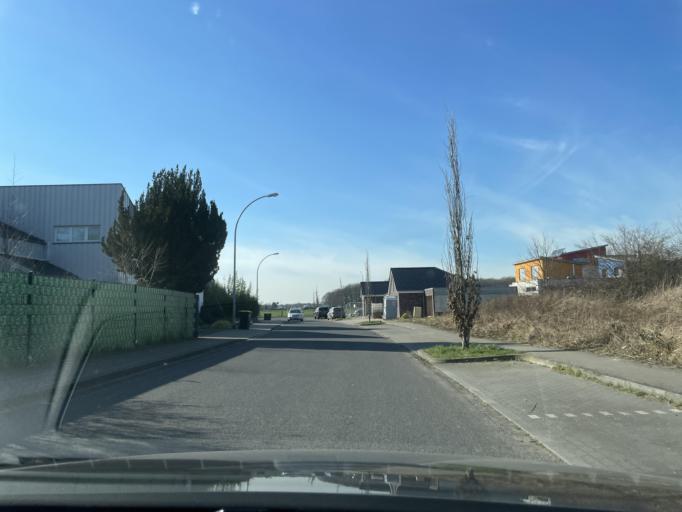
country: DE
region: North Rhine-Westphalia
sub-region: Regierungsbezirk Dusseldorf
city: Schwalmtal
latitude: 51.2087
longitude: 6.3322
